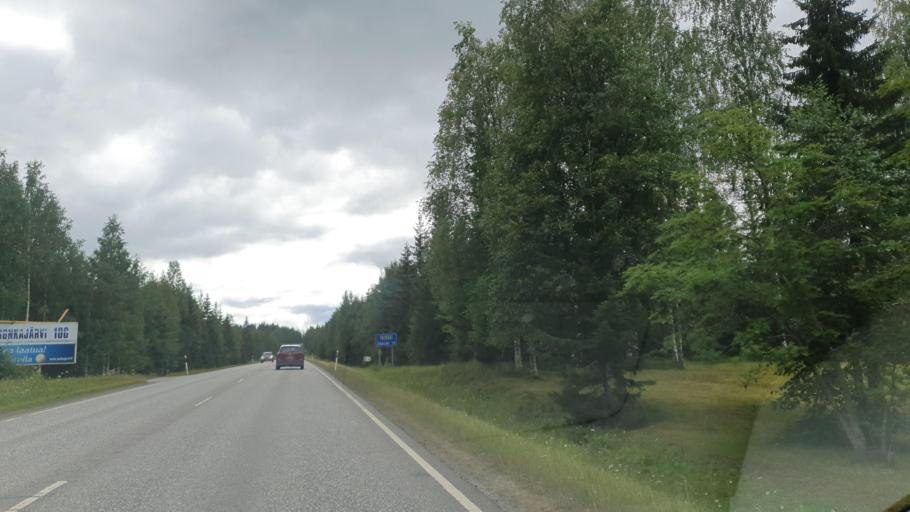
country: FI
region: Northern Savo
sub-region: Ylae-Savo
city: Sonkajaervi
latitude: 63.6927
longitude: 27.3501
